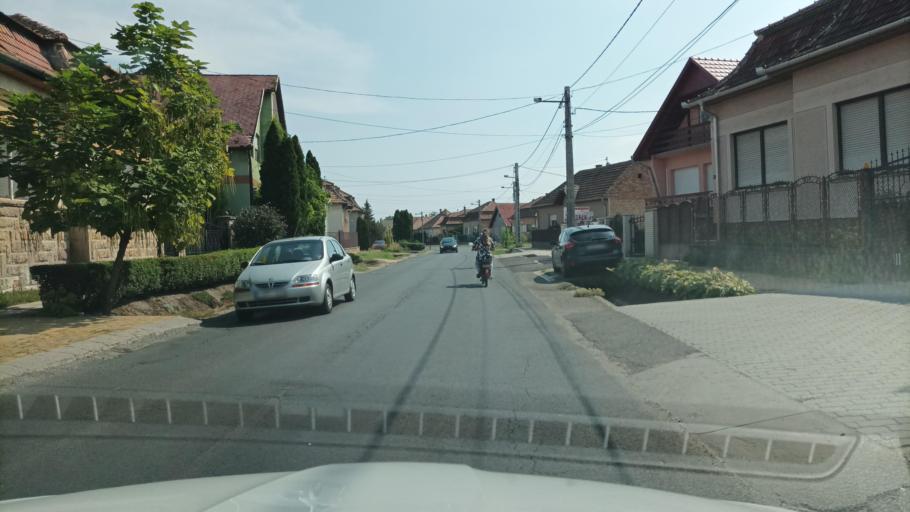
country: HU
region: Pest
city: Galgaheviz
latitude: 47.6206
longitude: 19.5604
